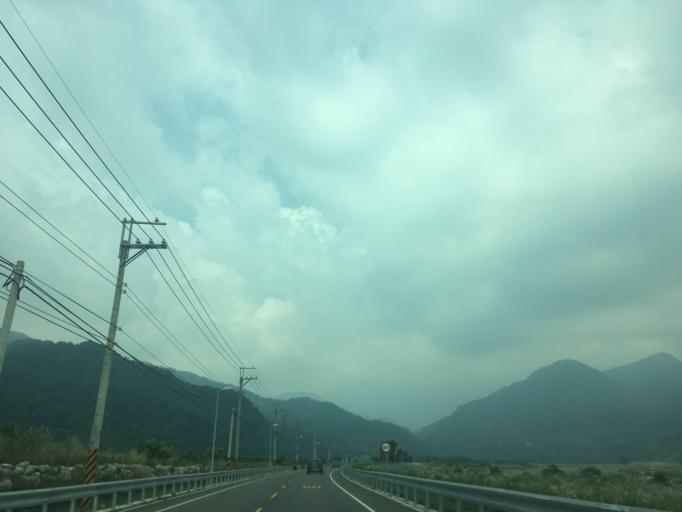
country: TW
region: Taiwan
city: Fengyuan
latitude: 24.2964
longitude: 120.8810
